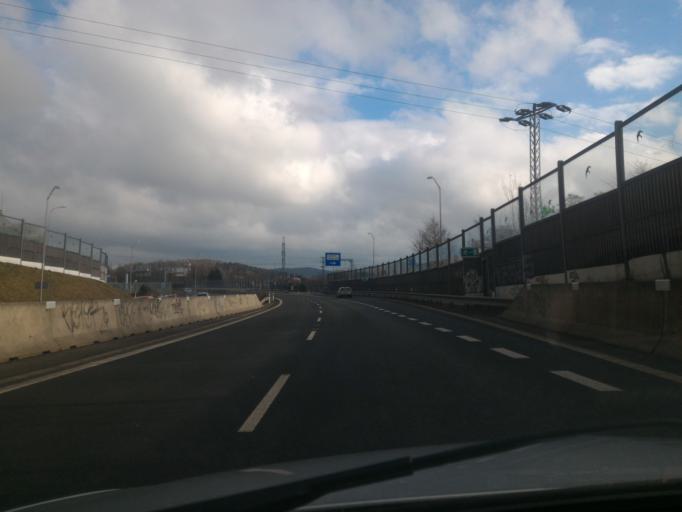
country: CZ
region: Liberecky
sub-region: Okres Liberec
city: Liberec
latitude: 50.7471
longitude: 15.0711
